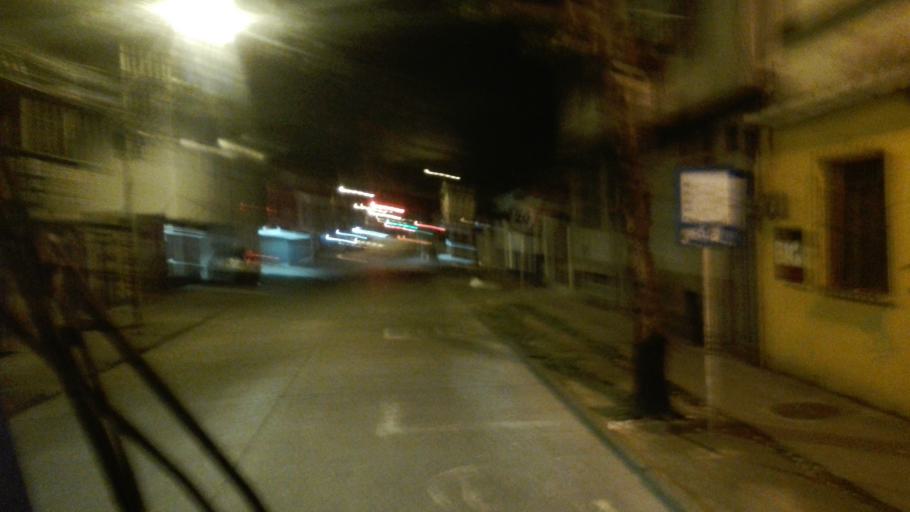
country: CO
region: Risaralda
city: Pereira
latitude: 4.8177
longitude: -75.6972
